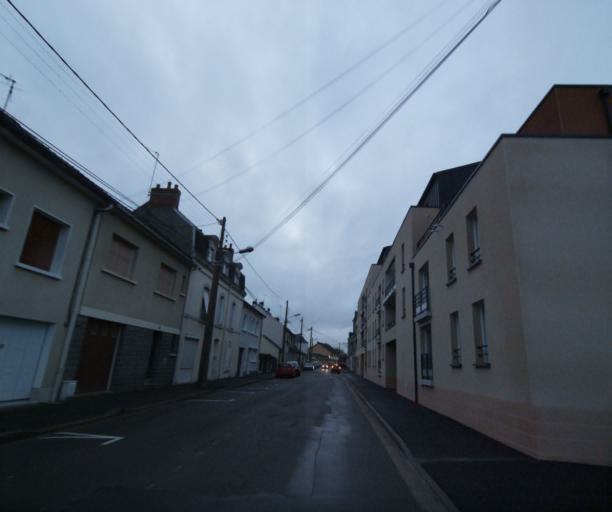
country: FR
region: Pays de la Loire
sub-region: Departement de la Sarthe
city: Coulaines
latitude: 48.0176
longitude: 0.1941
